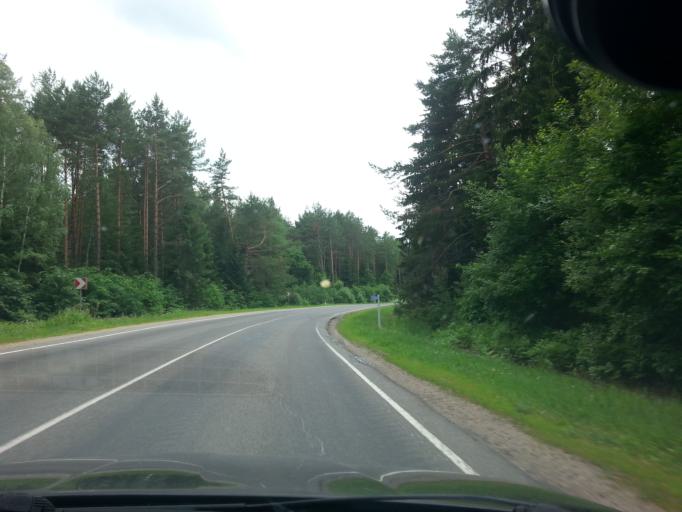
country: BY
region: Minsk
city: Svir
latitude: 54.8388
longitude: 26.1989
